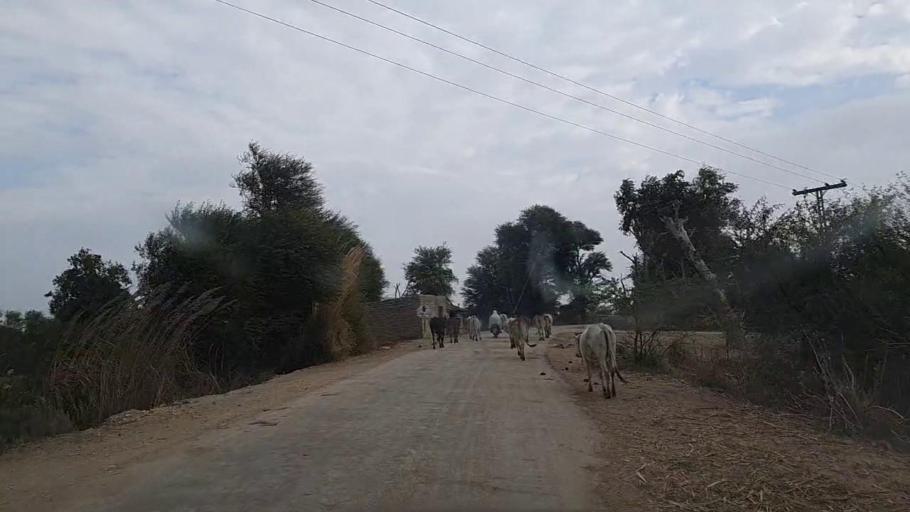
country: PK
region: Sindh
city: Sanghar
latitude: 26.2297
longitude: 68.9973
